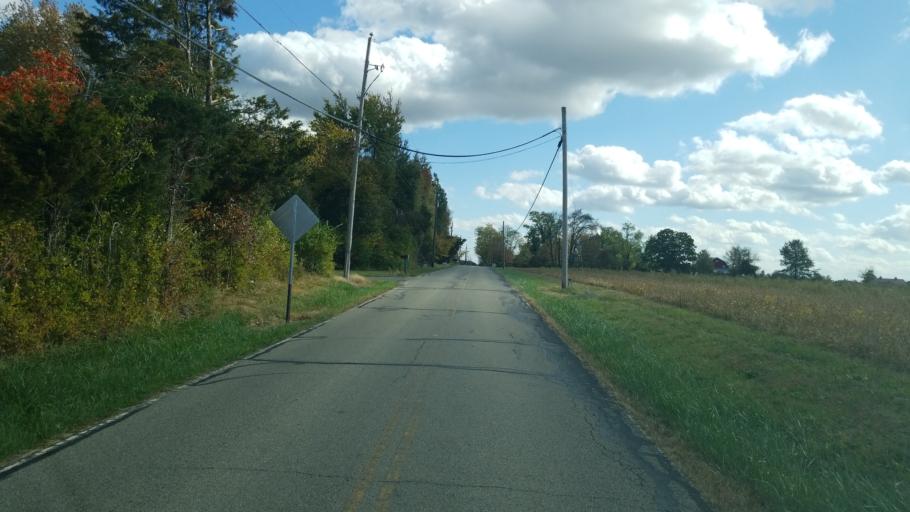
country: US
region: Ohio
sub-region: Warren County
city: South Lebanon
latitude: 39.3876
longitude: -84.1658
